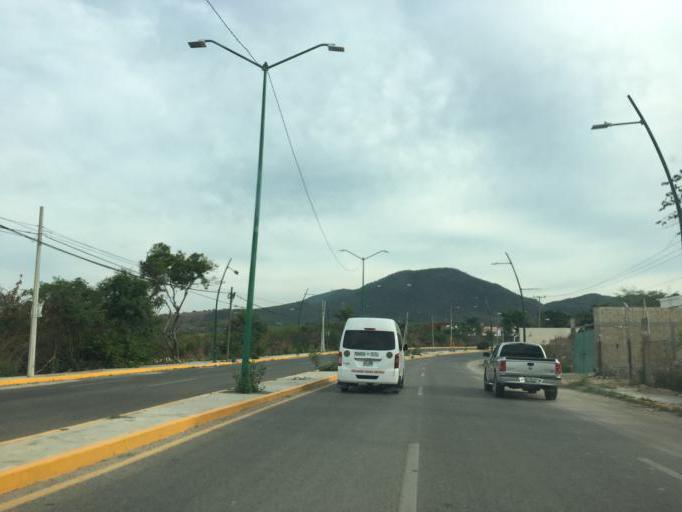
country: MX
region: Chiapas
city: Tuxtla Gutierrez
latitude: 16.7709
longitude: -93.1727
